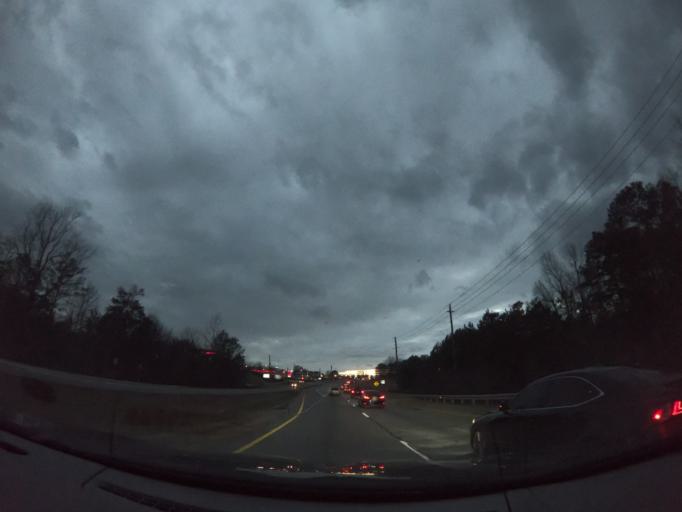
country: US
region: Georgia
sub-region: Cherokee County
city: Woodstock
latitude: 34.0875
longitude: -84.4768
